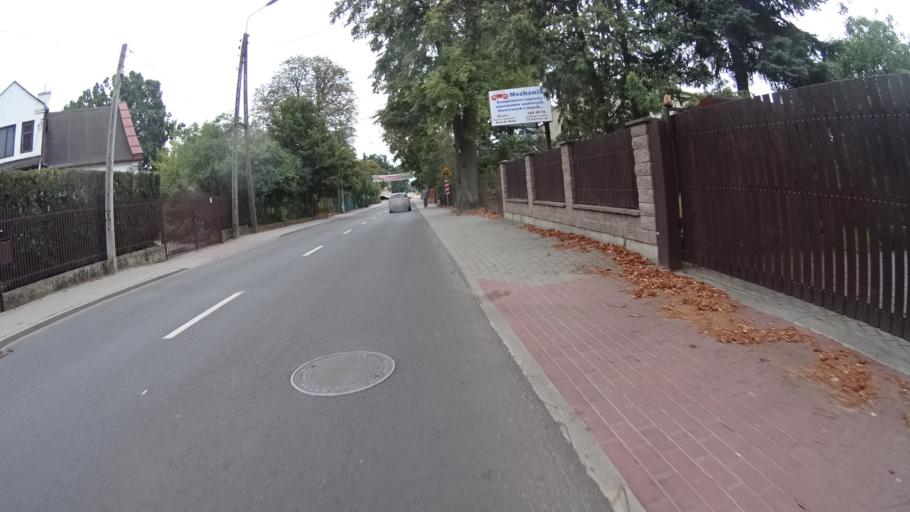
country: PL
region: Masovian Voivodeship
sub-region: Powiat pruszkowski
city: Granica
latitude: 52.1415
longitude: 20.7938
